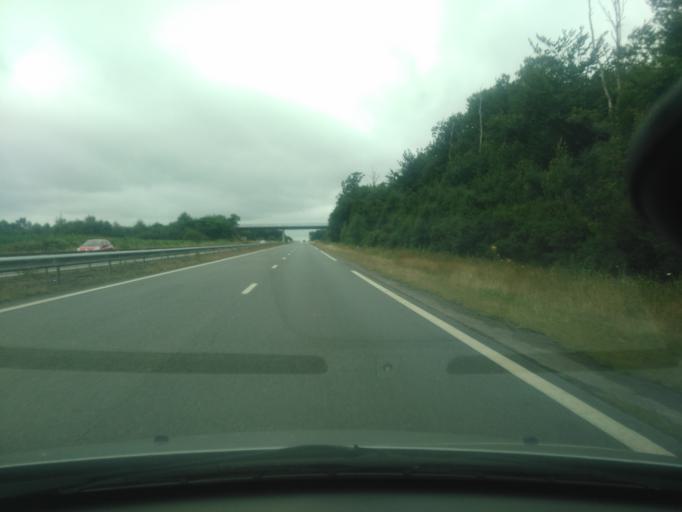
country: FR
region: Brittany
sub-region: Departement des Cotes-d'Armor
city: Plelan-le-Petit
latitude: 48.4235
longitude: -2.2496
